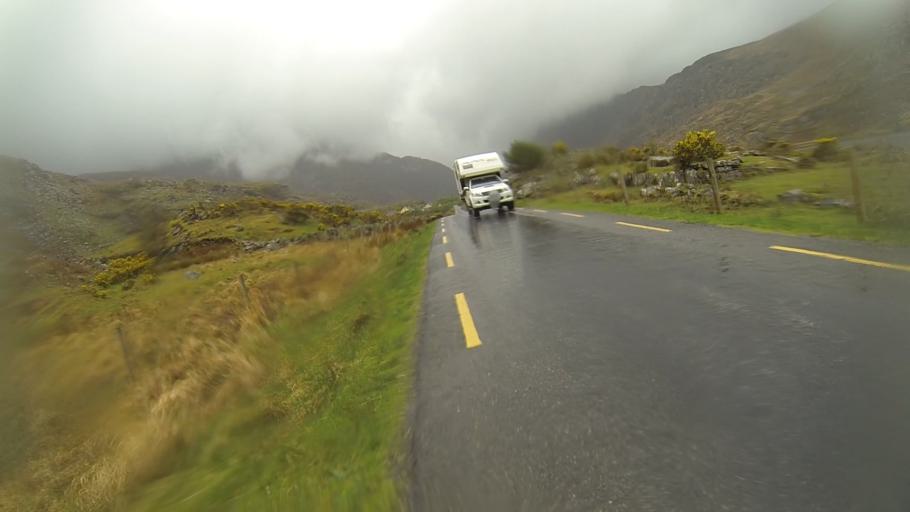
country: IE
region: Munster
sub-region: Ciarrai
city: Cill Airne
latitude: 52.0273
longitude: -9.6353
